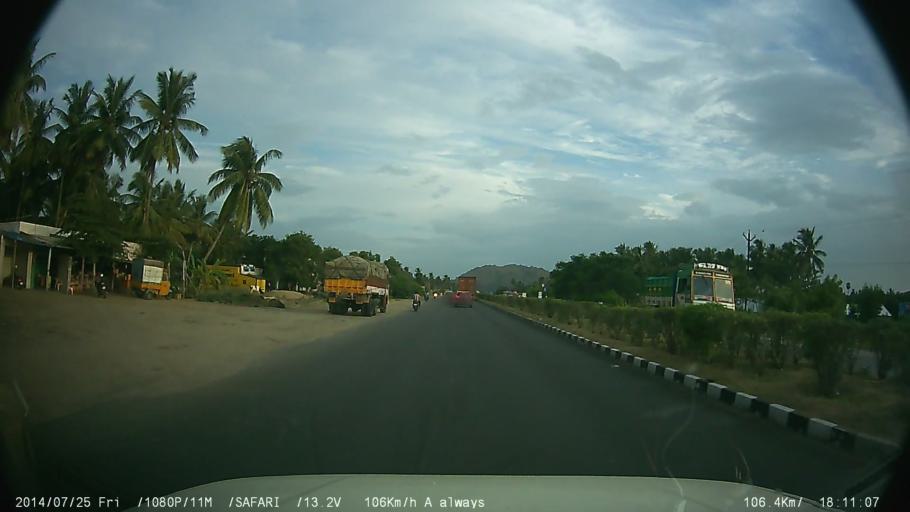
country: IN
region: Tamil Nadu
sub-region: Krishnagiri
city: Kaverippattanam
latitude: 12.3668
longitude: 78.2149
